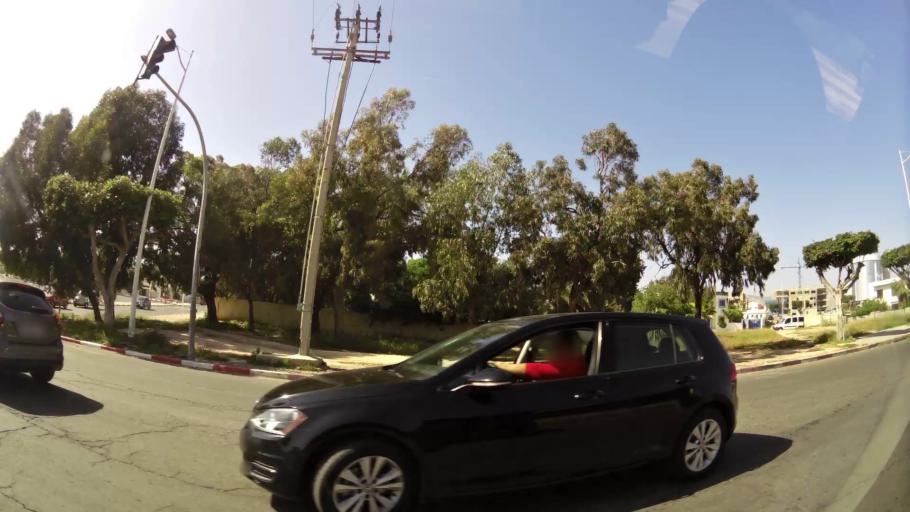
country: MA
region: Souss-Massa-Draa
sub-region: Agadir-Ida-ou-Tnan
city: Agadir
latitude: 30.4210
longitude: -9.5851
